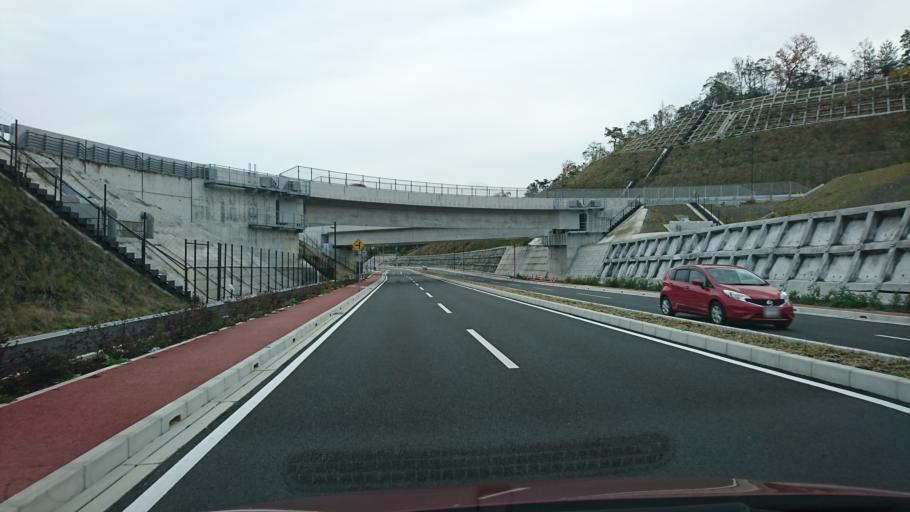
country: JP
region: Hyogo
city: Kawanishi
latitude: 34.8853
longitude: 135.3947
